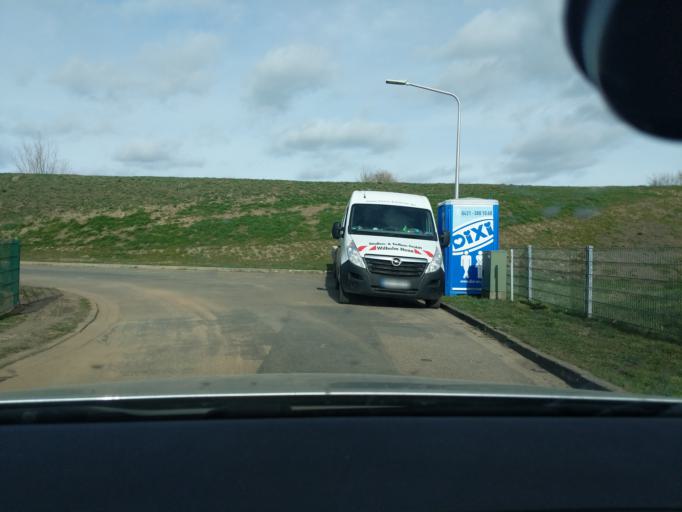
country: DE
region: Lower Saxony
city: Drochtersen
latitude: 53.7143
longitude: 9.3888
